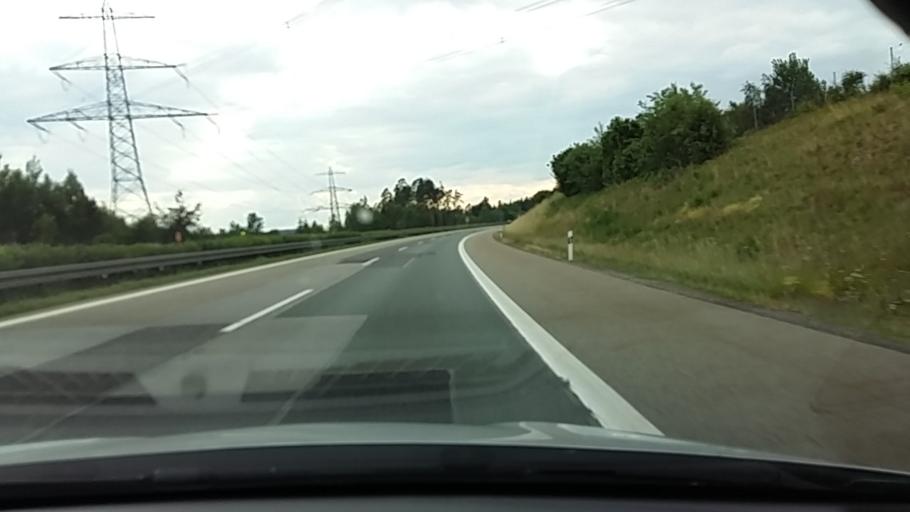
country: DE
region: Bavaria
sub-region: Upper Palatinate
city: Waidhaus
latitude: 49.6316
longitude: 12.5036
